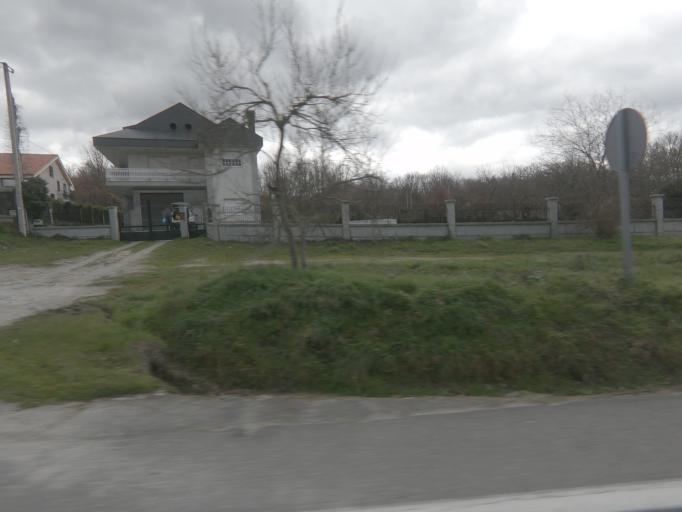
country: ES
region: Galicia
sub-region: Provincia de Ourense
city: Allariz
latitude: 42.1939
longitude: -7.7963
